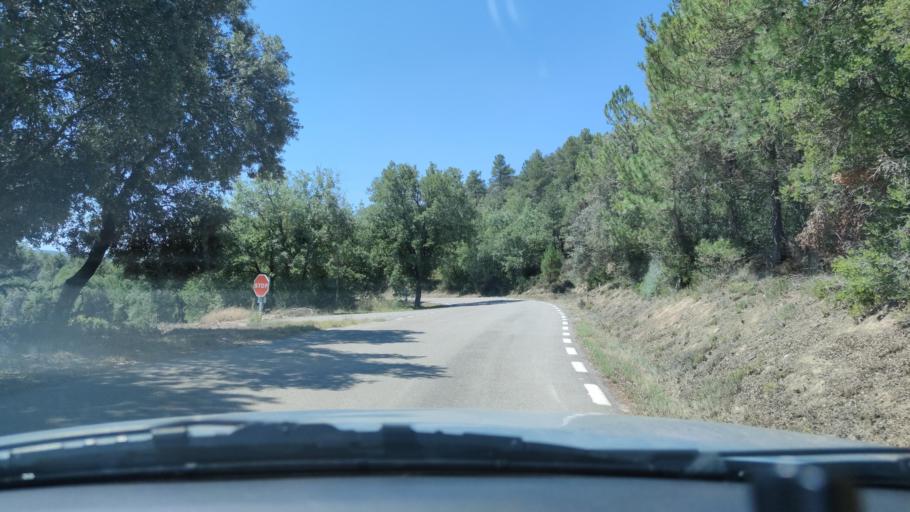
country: ES
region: Catalonia
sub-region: Provincia de Lleida
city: Tora de Riubregos
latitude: 41.8468
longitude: 1.4251
